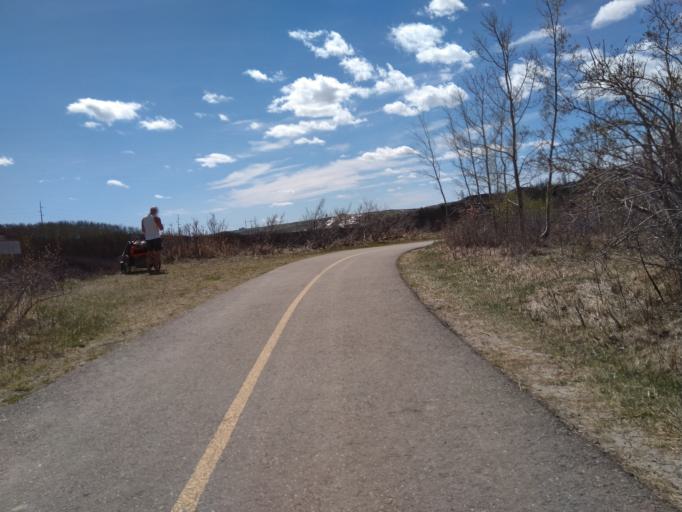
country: CA
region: Alberta
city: Calgary
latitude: 51.1233
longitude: -114.2374
